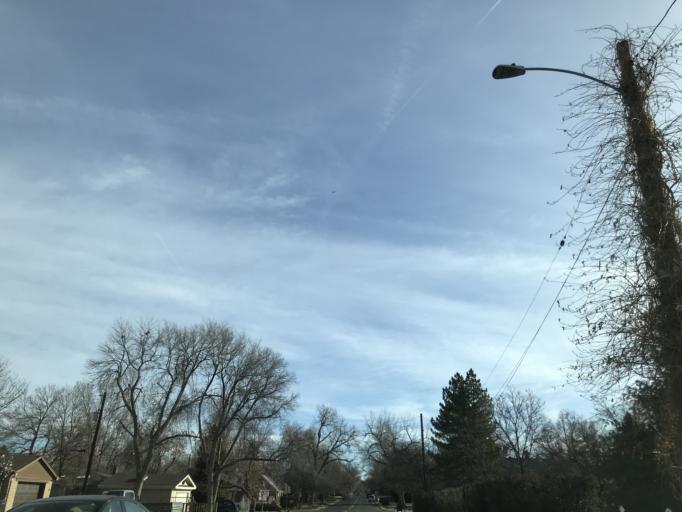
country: US
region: Colorado
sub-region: Arapahoe County
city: Littleton
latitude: 39.6024
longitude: -105.0152
